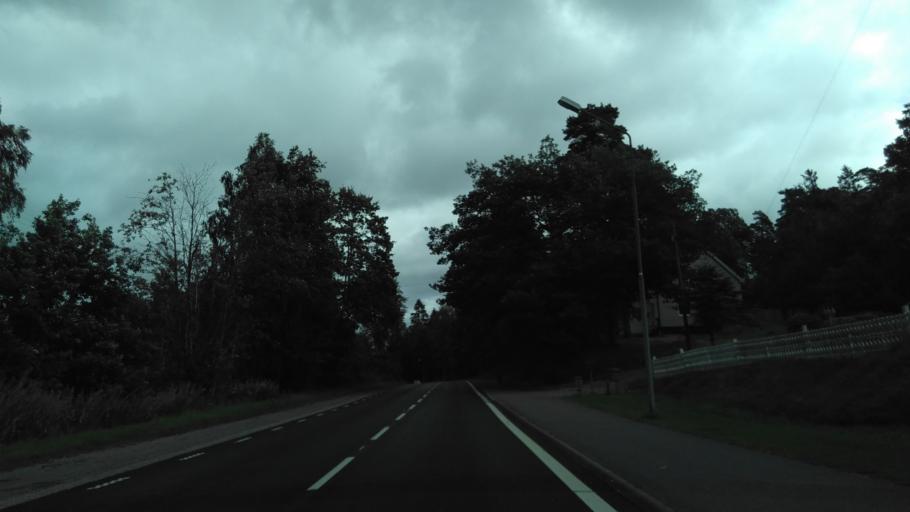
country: SE
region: Vaestra Goetaland
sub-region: Boras Kommun
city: Viskafors
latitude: 57.6319
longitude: 12.8512
